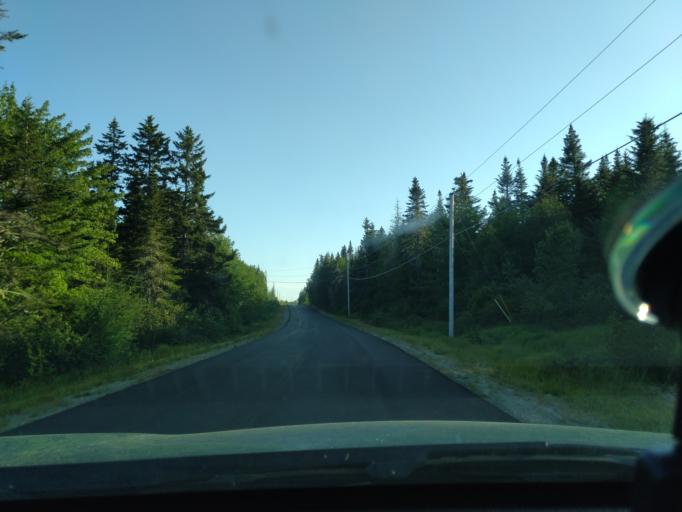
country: US
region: Maine
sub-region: Washington County
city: East Machias
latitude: 44.6932
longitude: -67.1644
